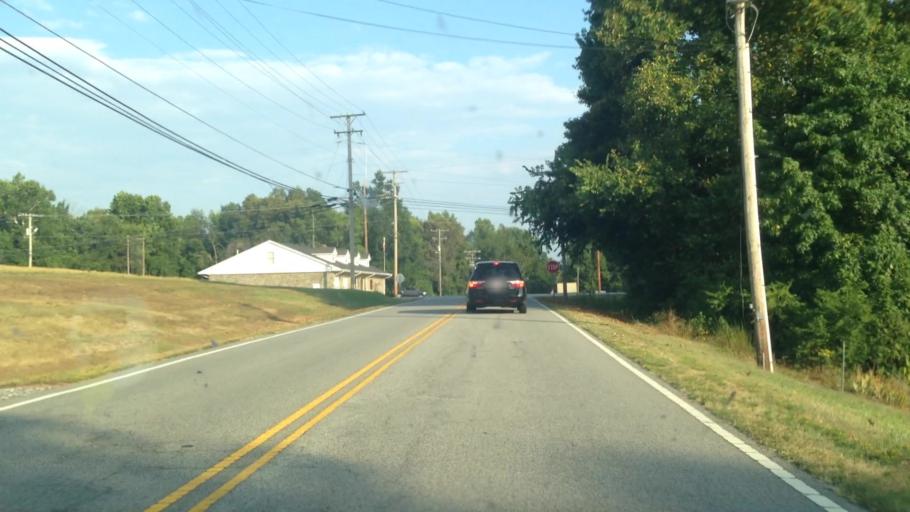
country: US
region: North Carolina
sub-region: Davidson County
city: Thomasville
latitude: 35.9407
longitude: -80.0726
